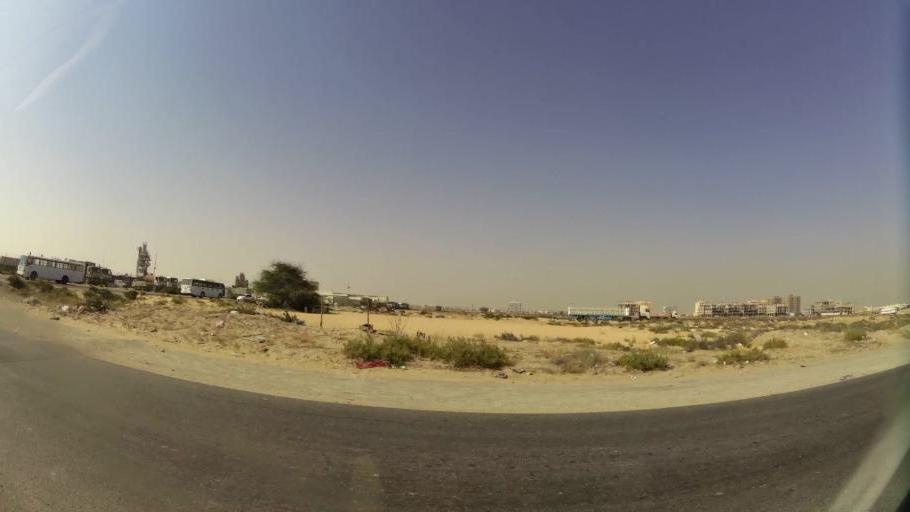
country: AE
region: Ajman
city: Ajman
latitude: 25.4308
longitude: 55.5423
